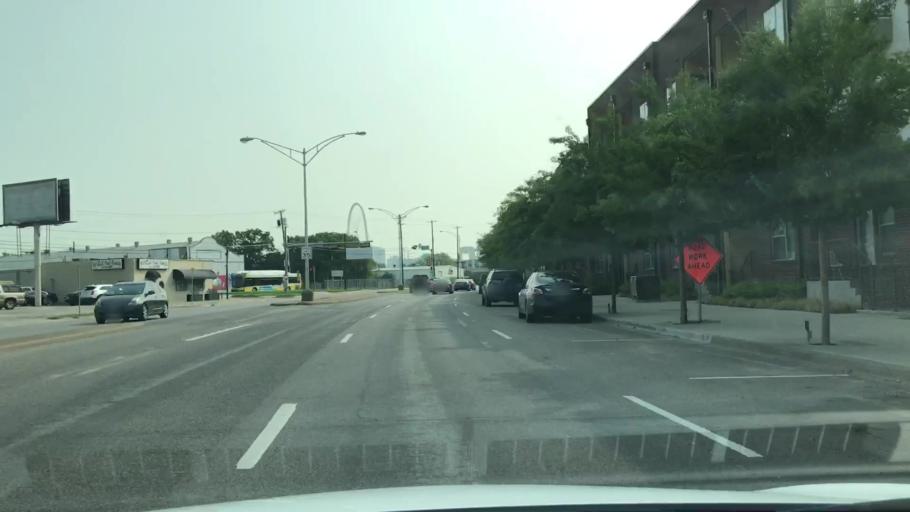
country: US
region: Texas
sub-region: Dallas County
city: Dallas
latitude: 32.7722
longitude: -96.8332
